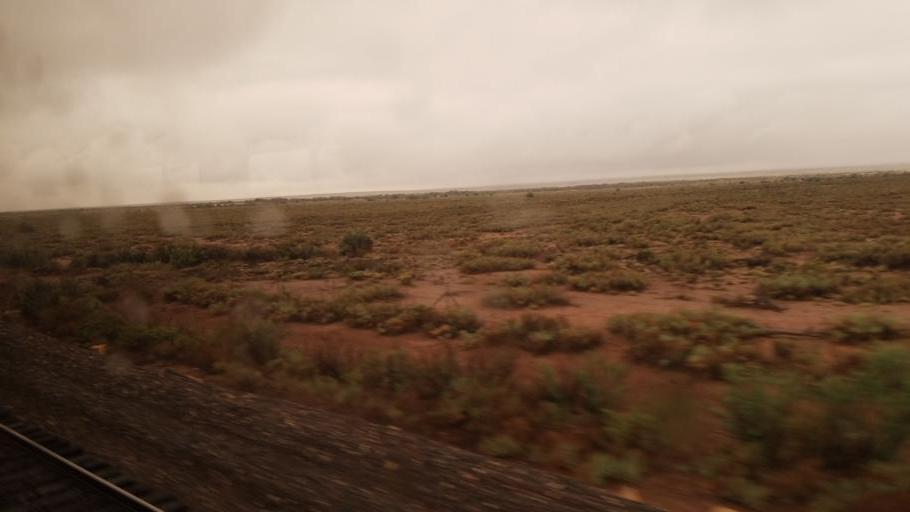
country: US
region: Arizona
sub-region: Navajo County
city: Winslow
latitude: 35.0012
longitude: -110.6343
